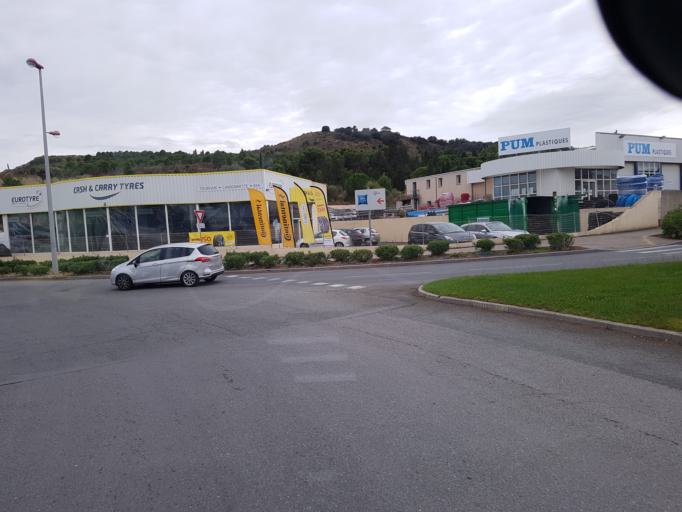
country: FR
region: Languedoc-Roussillon
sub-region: Departement de l'Aude
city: Narbonne
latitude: 43.1579
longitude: 2.9778
